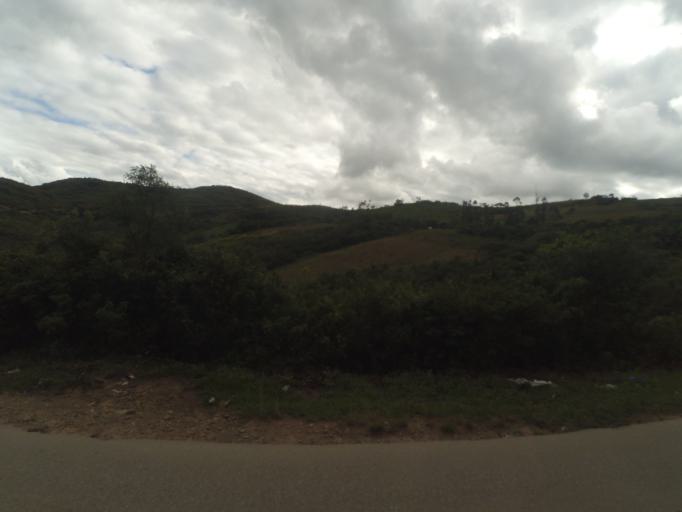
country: BO
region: Santa Cruz
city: Samaipata
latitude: -18.1743
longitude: -63.8513
